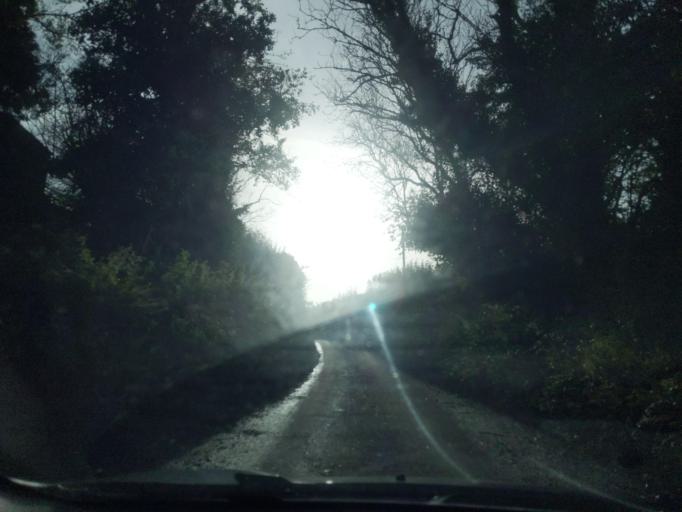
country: GB
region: England
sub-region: Cornwall
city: Pillaton
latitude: 50.3712
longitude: -4.2948
